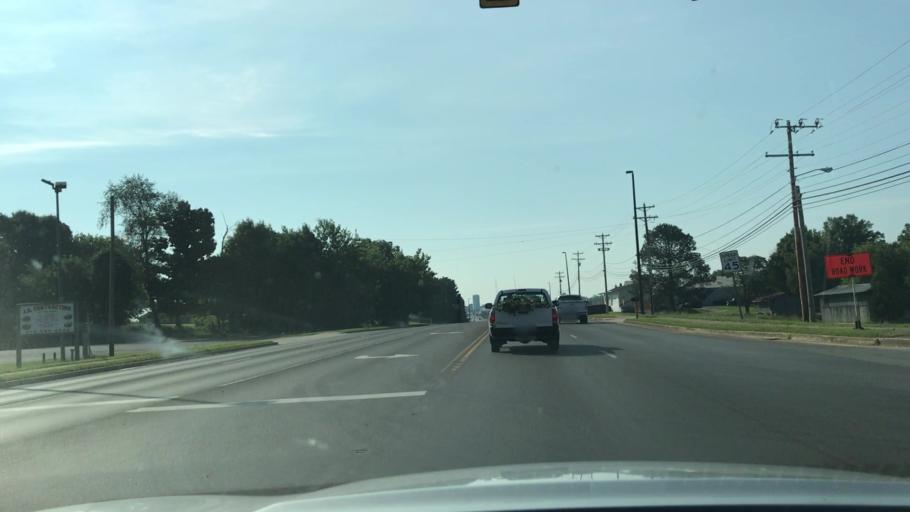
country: US
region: Kentucky
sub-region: Barren County
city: Glasgow
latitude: 37.0072
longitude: -85.9346
